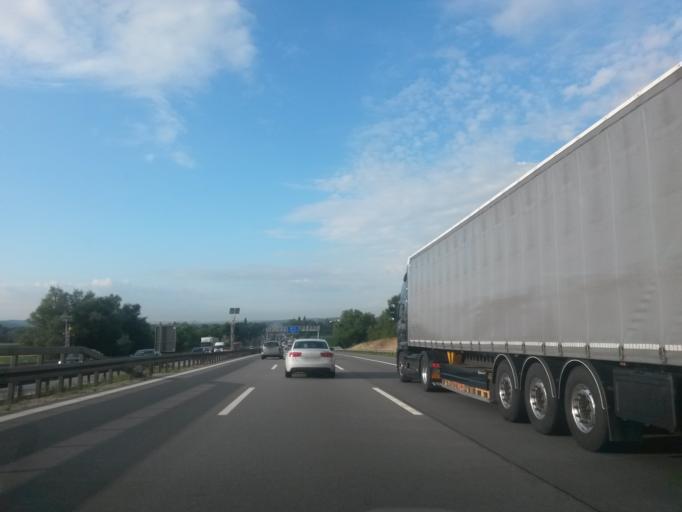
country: DE
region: Bavaria
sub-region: Upper Bavaria
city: Allershausen
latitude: 48.4423
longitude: 11.5892
